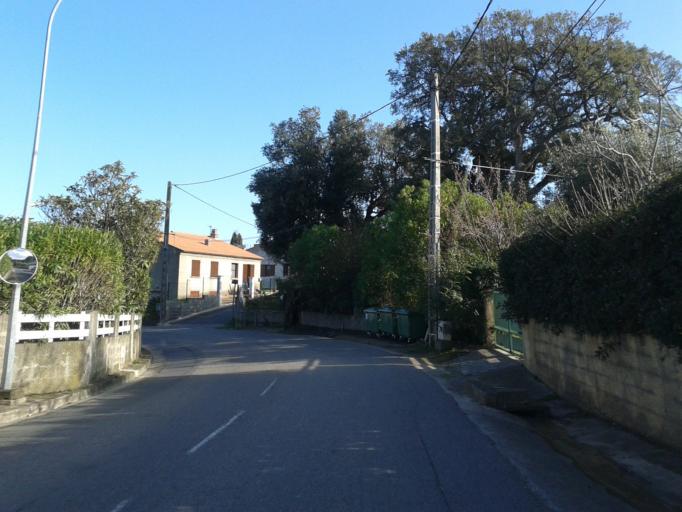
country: FR
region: Corsica
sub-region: Departement de la Haute-Corse
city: Biguglia
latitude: 42.5914
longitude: 9.4276
